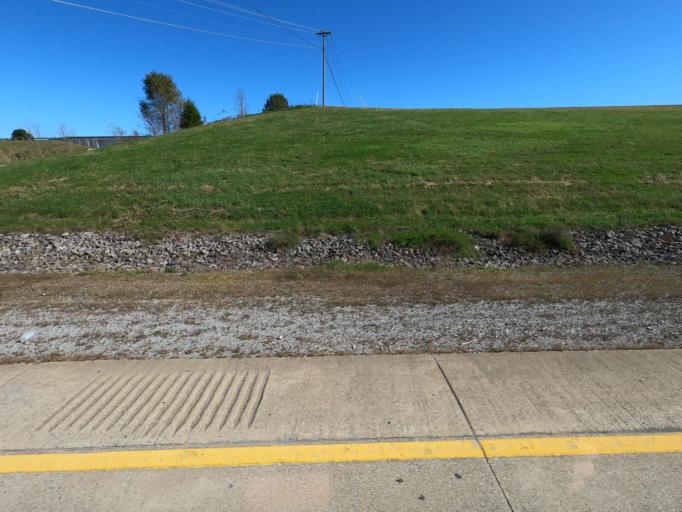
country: US
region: Tennessee
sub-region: Williamson County
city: Fairview
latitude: 35.9386
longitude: -87.1911
